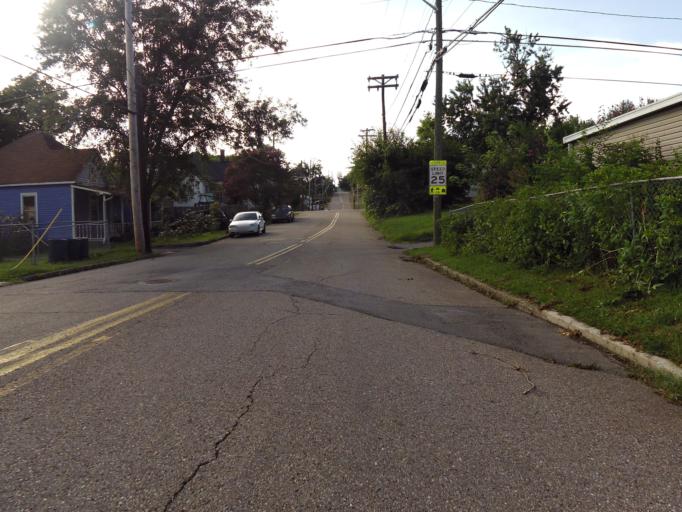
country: US
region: Tennessee
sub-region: Knox County
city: Knoxville
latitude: 35.9882
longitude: -83.9283
